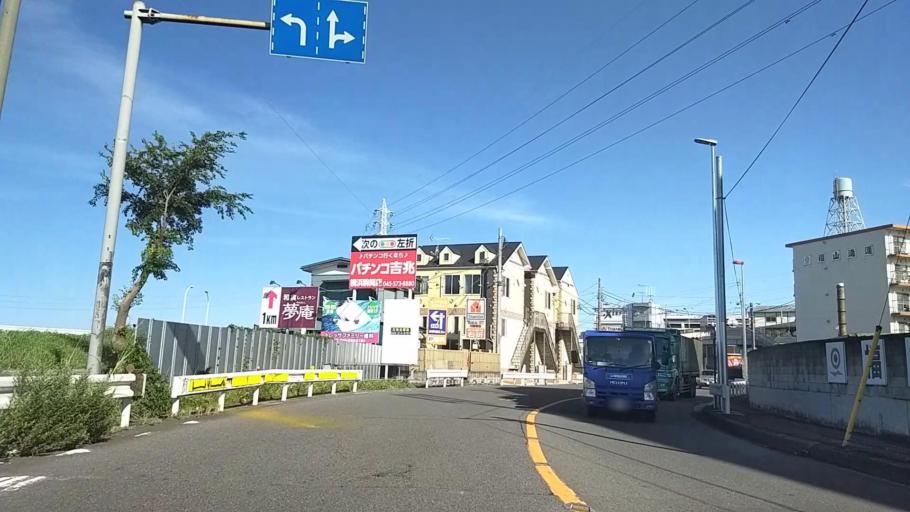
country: JP
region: Kanagawa
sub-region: Kawasaki-shi
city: Kawasaki
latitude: 35.5335
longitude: 139.6676
